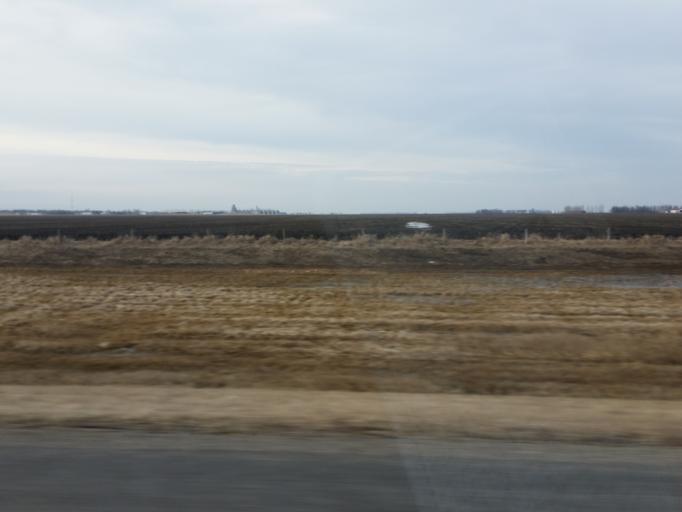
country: US
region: North Dakota
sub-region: Cass County
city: Casselton
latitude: 46.8768
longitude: -97.1875
